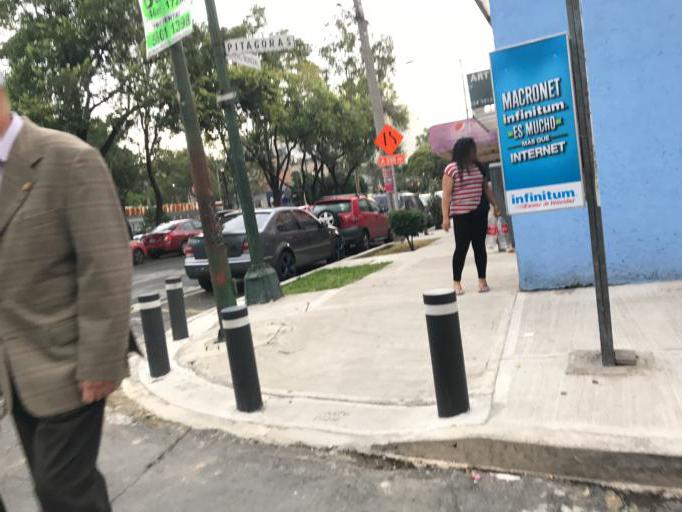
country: MX
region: Mexico City
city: Benito Juarez
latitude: 19.4015
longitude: -99.1571
